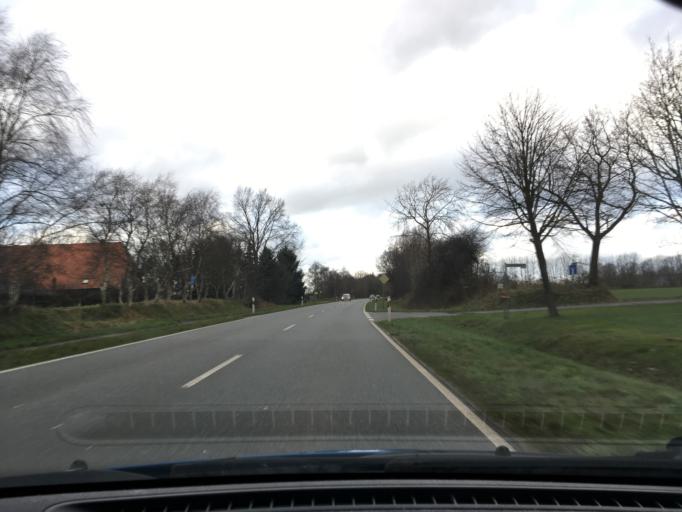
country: DE
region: Schleswig-Holstein
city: Kaisborstel
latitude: 54.0192
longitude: 9.4772
